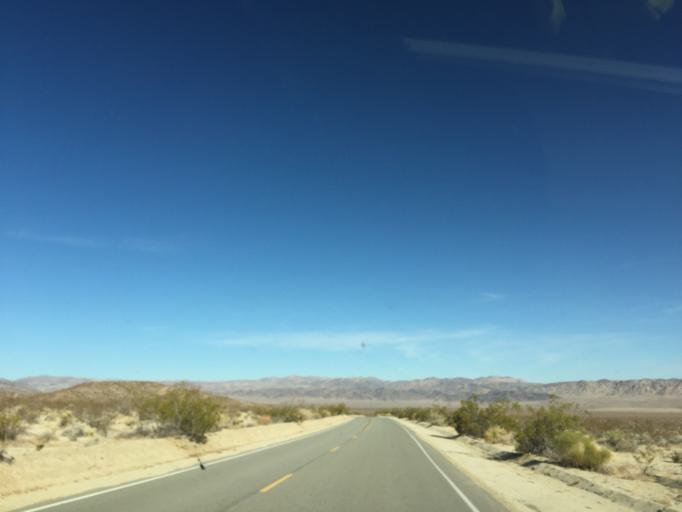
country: US
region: California
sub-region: San Bernardino County
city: Twentynine Palms
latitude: 33.8782
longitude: -115.8124
